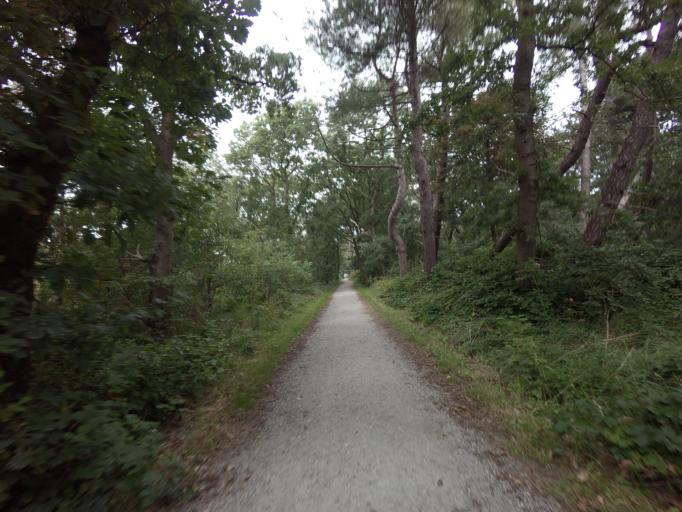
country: NL
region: Friesland
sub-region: Gemeente Schiermonnikoog
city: Schiermonnikoog
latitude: 53.4848
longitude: 6.1635
